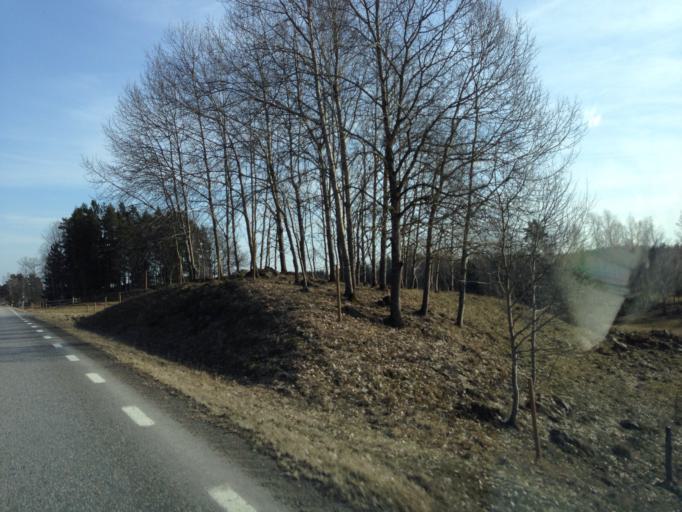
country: SE
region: Soedermanland
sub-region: Flens Kommun
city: Flen
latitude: 59.0628
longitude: 16.6424
